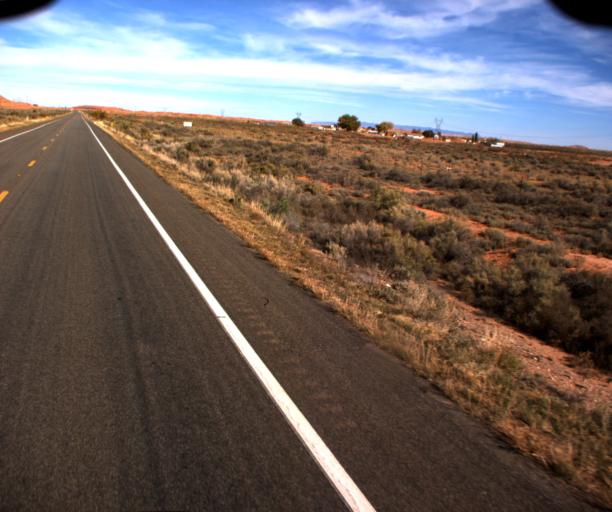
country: US
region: Arizona
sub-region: Navajo County
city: Kayenta
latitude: 36.8176
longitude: -109.8837
